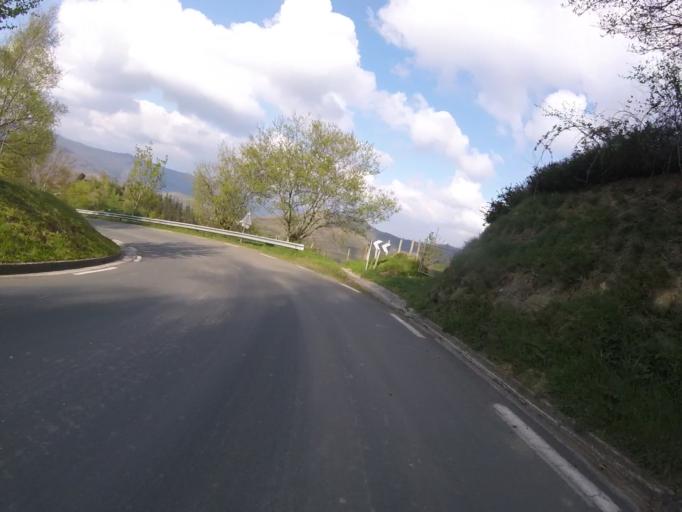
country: ES
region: Basque Country
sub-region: Provincia de Guipuzcoa
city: Azkoitia
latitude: 43.2084
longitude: -2.3345
